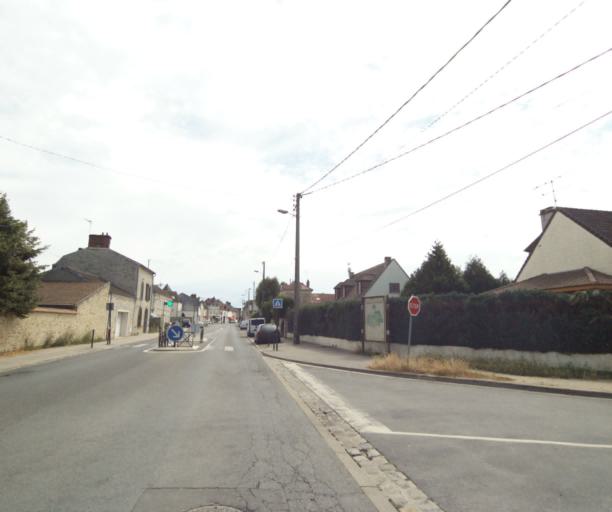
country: FR
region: Ile-de-France
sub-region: Departement de Seine-et-Marne
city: Chailly-en-Biere
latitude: 48.4680
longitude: 2.6056
